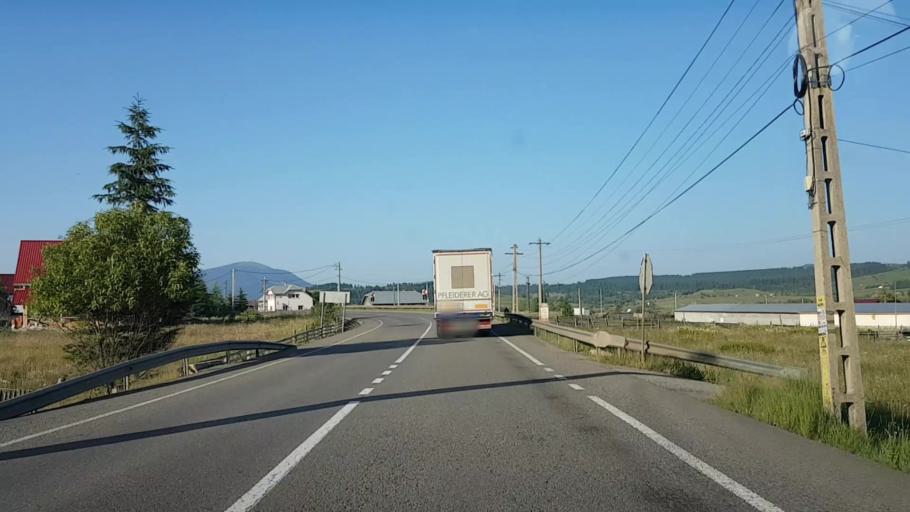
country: RO
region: Suceava
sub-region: Comuna Poiana Stampei
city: Poiana Stampei
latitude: 47.3087
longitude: 25.1257
